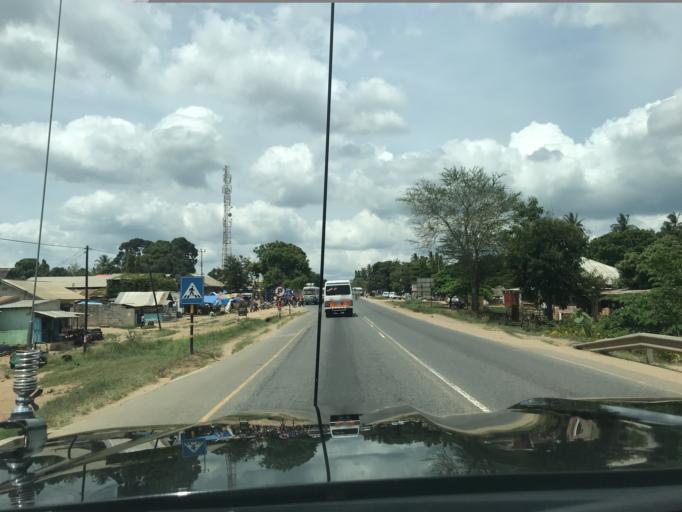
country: TZ
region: Pwani
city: Kibaha
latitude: -6.7392
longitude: 38.8717
